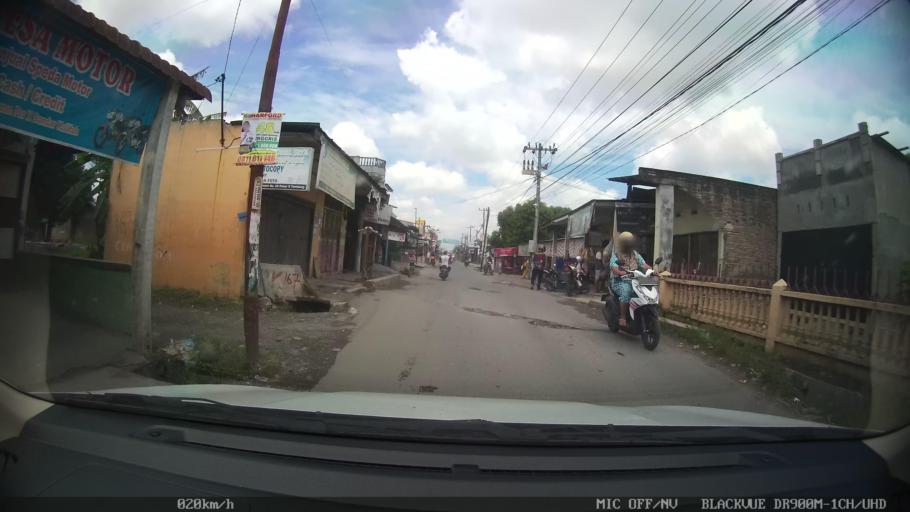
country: ID
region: North Sumatra
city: Medan
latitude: 3.6073
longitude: 98.7564
